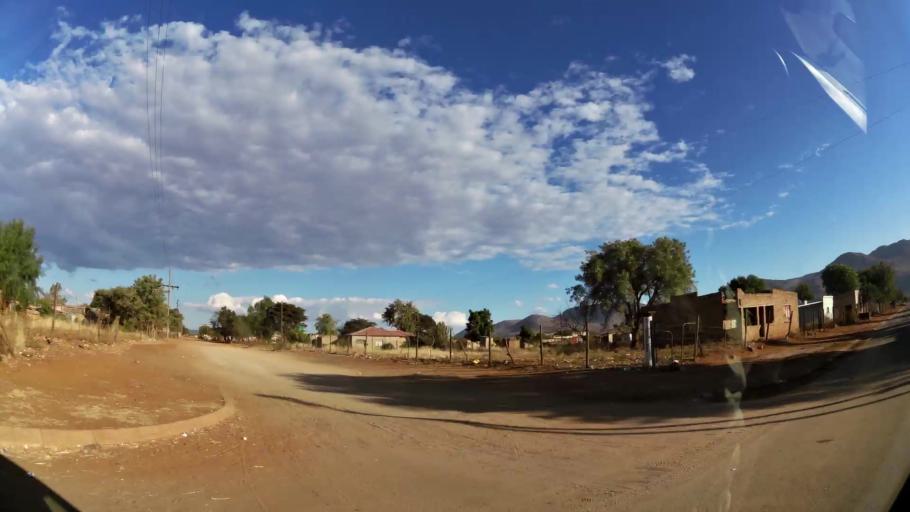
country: ZA
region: Limpopo
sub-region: Waterberg District Municipality
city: Mokopane
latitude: -24.1723
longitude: 28.9764
